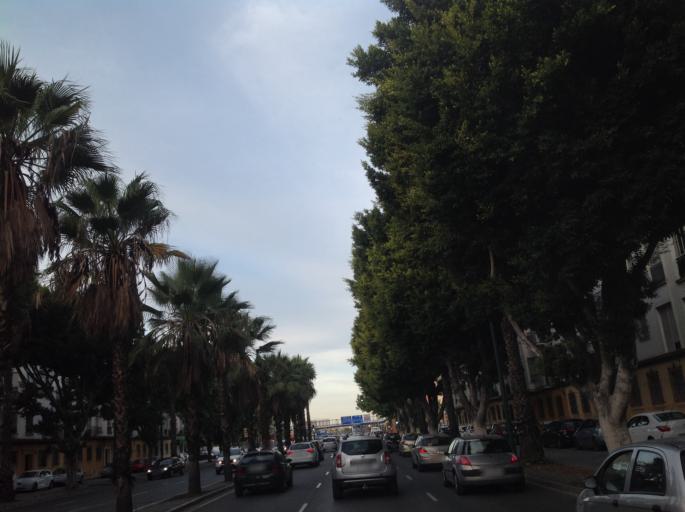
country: ES
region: Andalusia
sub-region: Provincia de Malaga
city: Malaga
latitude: 36.7154
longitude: -4.4466
